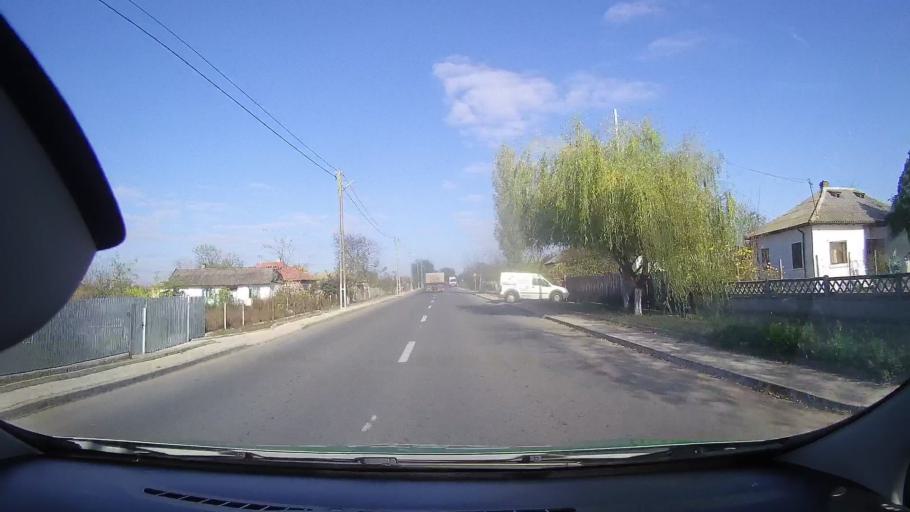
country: RO
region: Tulcea
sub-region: Comuna Mahmudia
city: Mahmudia
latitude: 45.0095
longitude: 29.0550
